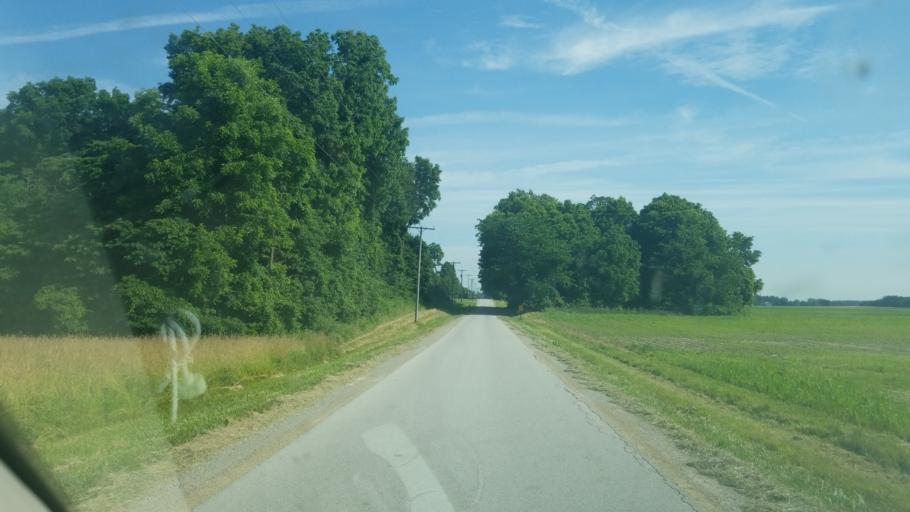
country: US
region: Ohio
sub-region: Wyandot County
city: Upper Sandusky
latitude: 40.8508
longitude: -83.2369
